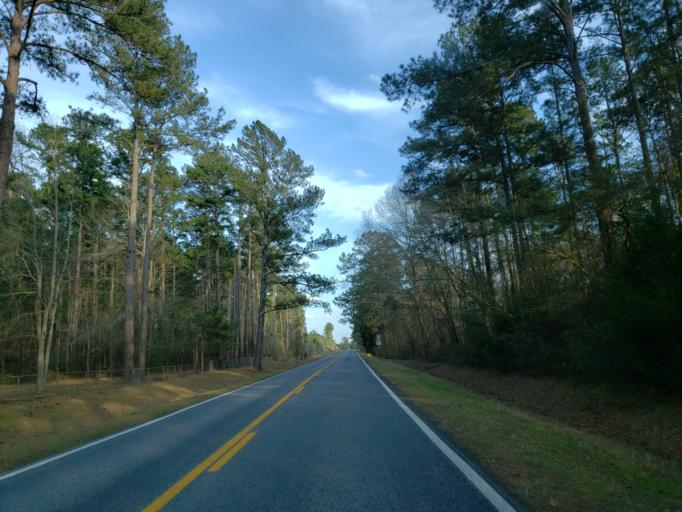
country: US
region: Mississippi
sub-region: Clarke County
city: Stonewall
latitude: 32.1774
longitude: -88.7979
